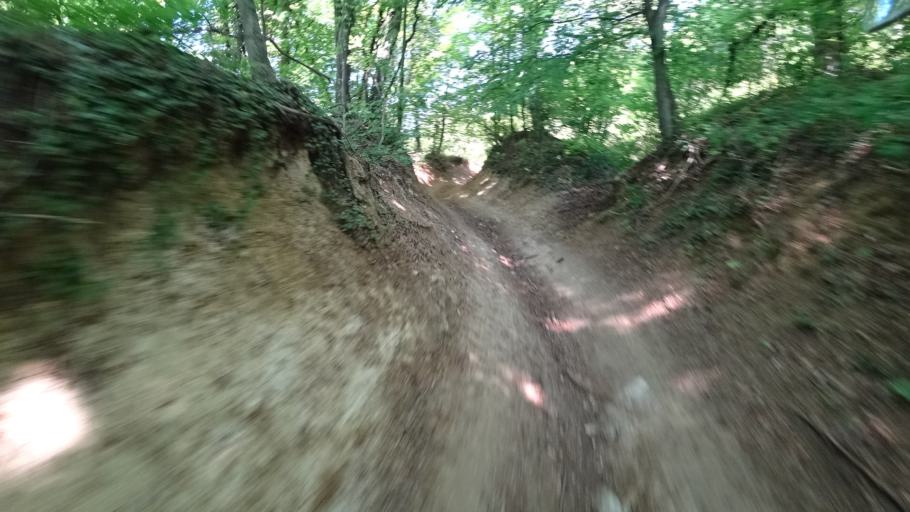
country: HR
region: Zagrebacka
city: Bestovje
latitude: 45.8338
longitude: 15.8347
